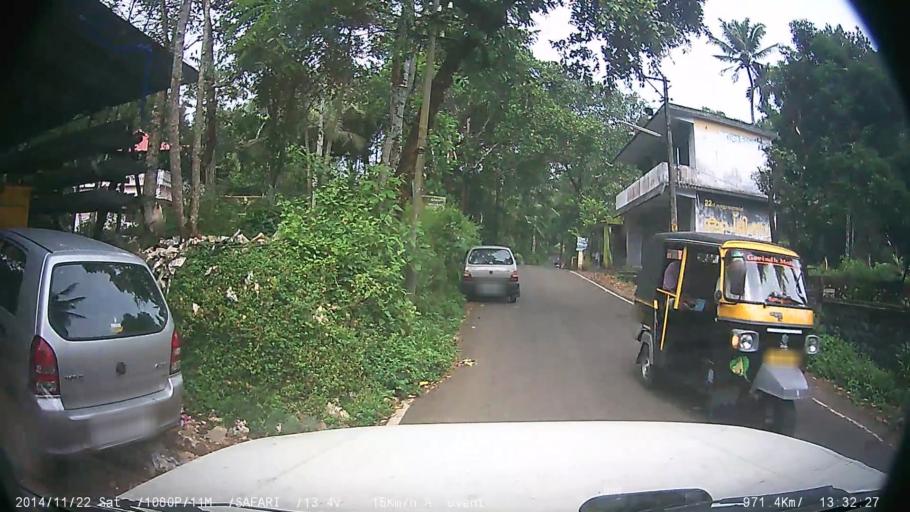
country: IN
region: Kerala
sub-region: Ernakulam
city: Piravam
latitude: 9.7926
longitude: 76.5274
